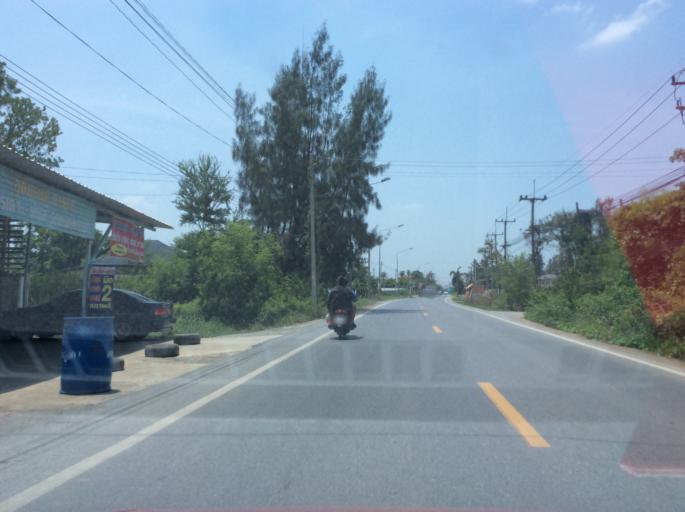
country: TH
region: Pathum Thani
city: Ban Rangsit
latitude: 14.0108
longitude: 100.7793
